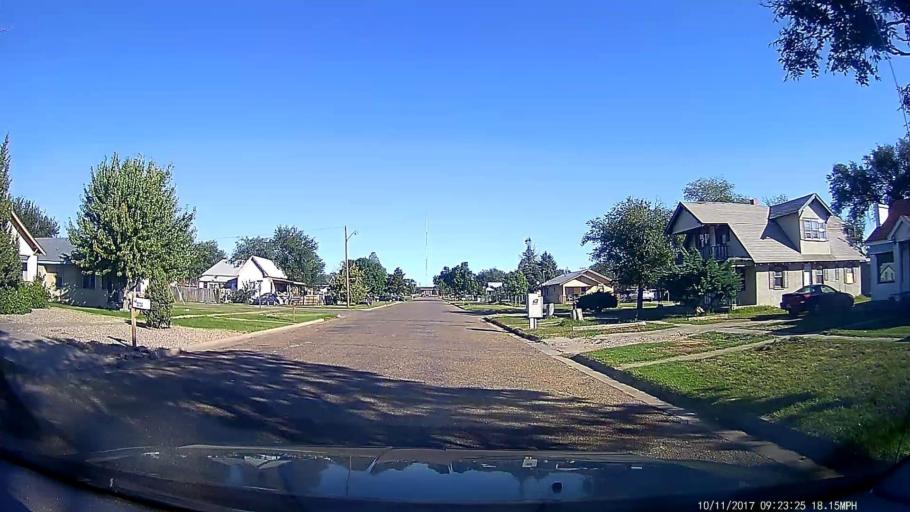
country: US
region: New Mexico
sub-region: Curry County
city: Clovis
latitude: 34.4083
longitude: -103.2077
